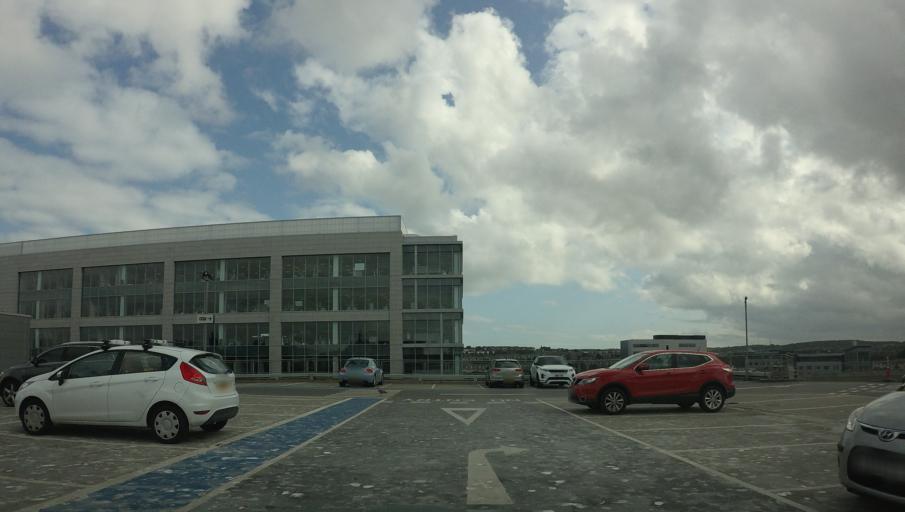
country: GB
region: Scotland
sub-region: Aberdeen City
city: Aberdeen
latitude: 57.1420
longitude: -2.0959
